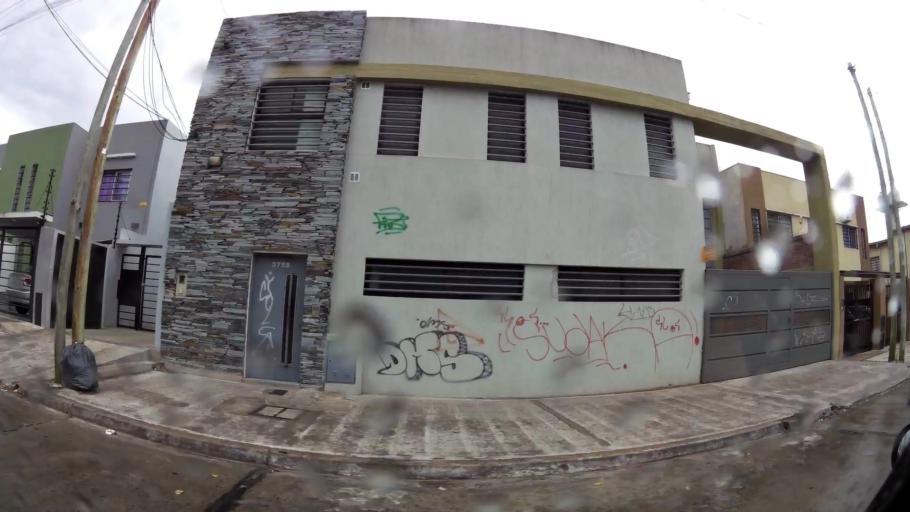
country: AR
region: Buenos Aires
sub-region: Partido de Quilmes
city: Quilmes
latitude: -34.7636
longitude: -58.2234
